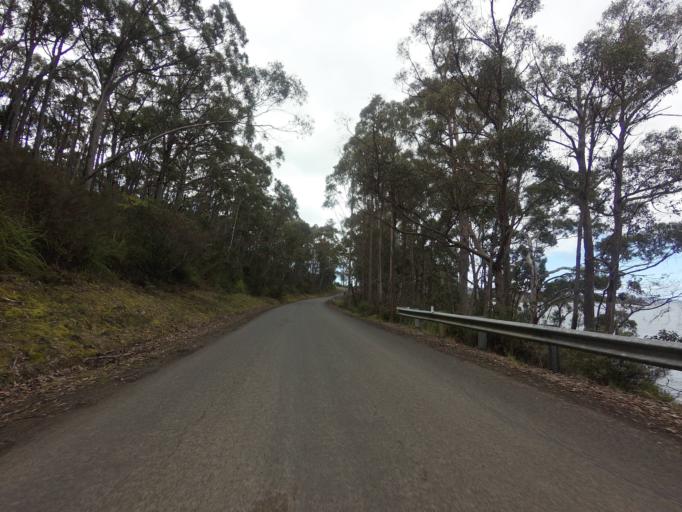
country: AU
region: Tasmania
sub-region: Huon Valley
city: Geeveston
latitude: -43.4353
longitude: 146.9648
